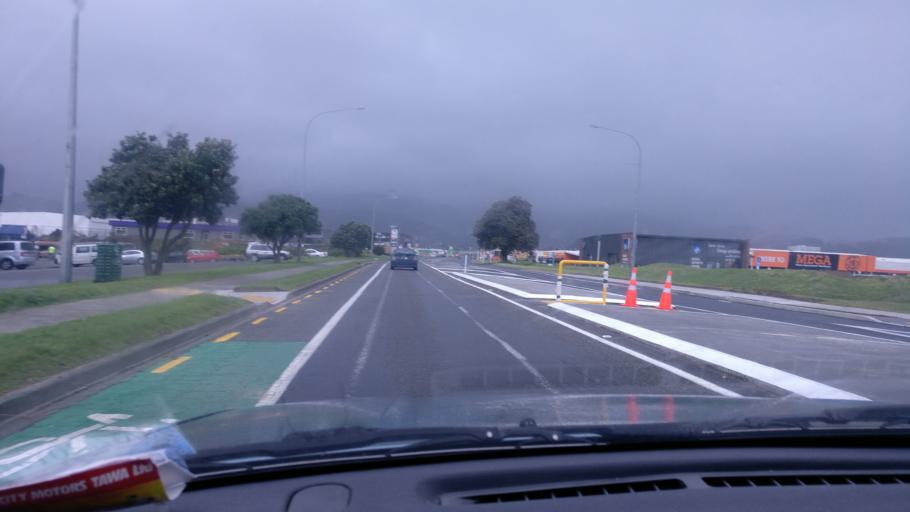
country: NZ
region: Wellington
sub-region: Kapiti Coast District
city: Paraparaumu
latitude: -40.9039
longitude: 174.9953
